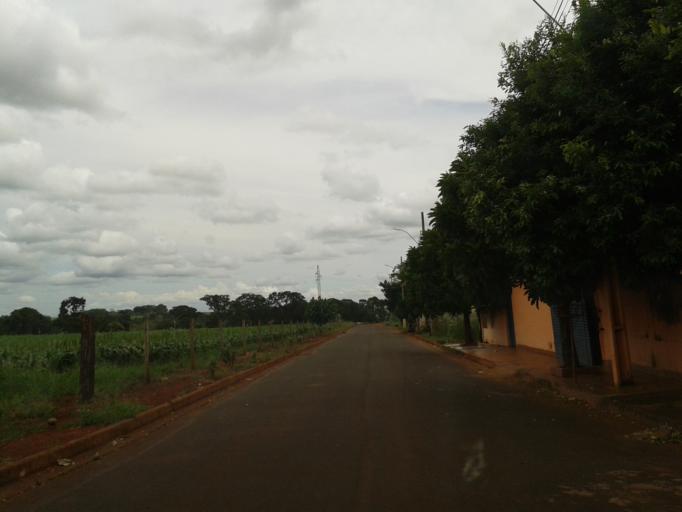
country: BR
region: Minas Gerais
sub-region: Centralina
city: Centralina
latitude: -18.5844
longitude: -49.2077
